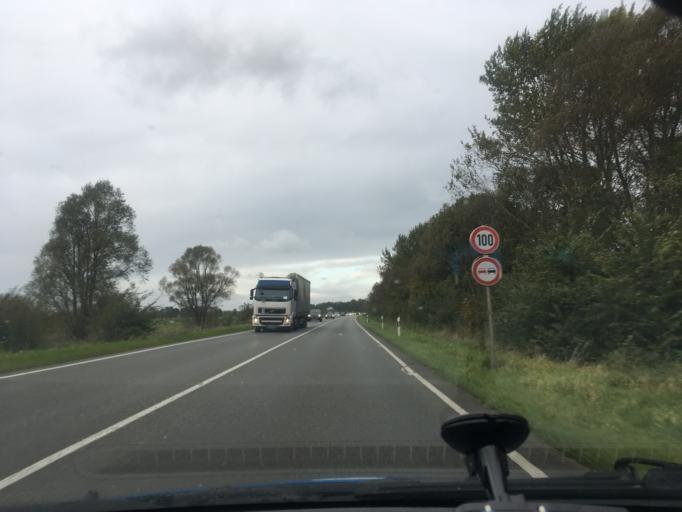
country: DE
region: Lower Saxony
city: Marschacht
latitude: 53.3982
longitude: 10.3323
